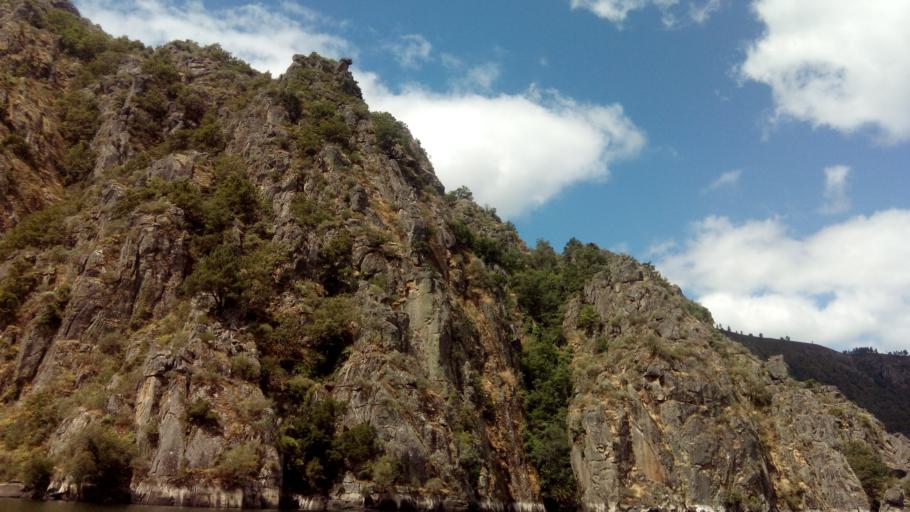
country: ES
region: Galicia
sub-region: Provincia de Lugo
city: Sober
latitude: 42.3897
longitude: -7.6215
